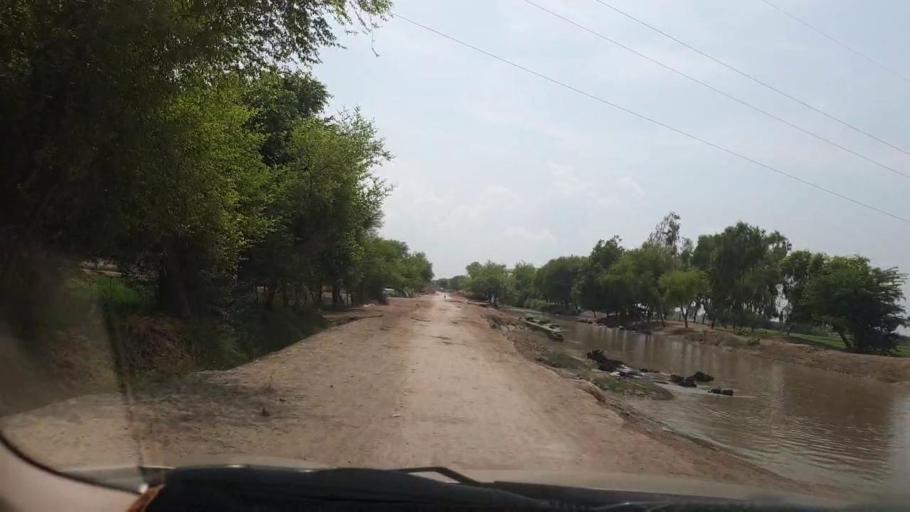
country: PK
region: Sindh
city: Larkana
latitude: 27.5823
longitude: 68.1151
